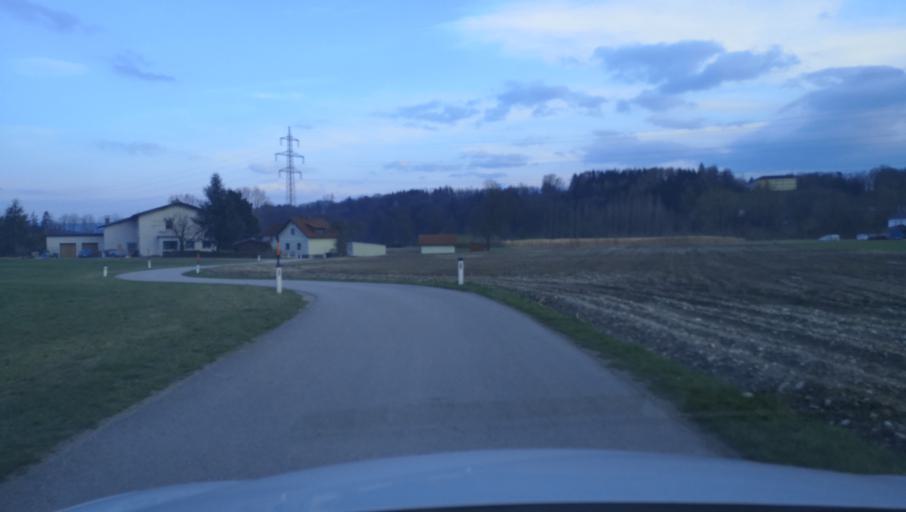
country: AT
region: Lower Austria
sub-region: Politischer Bezirk Amstetten
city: Amstetten
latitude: 48.1054
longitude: 14.9010
